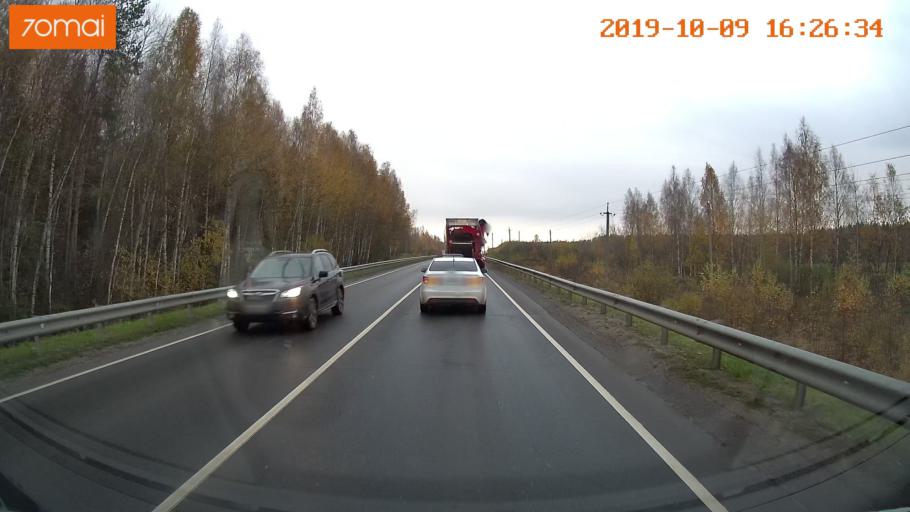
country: RU
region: Kostroma
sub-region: Kostromskoy Rayon
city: Kostroma
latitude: 57.6371
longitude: 40.9245
